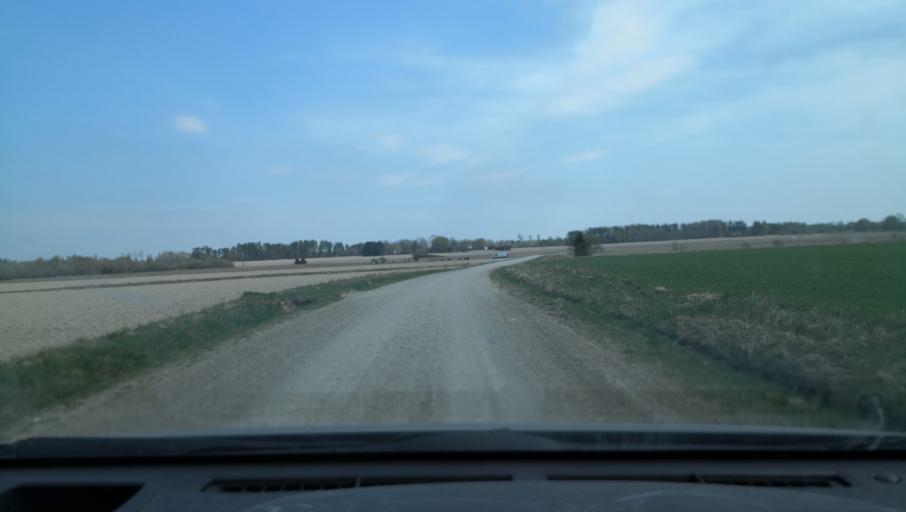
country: SE
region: Vaestmanland
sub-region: Vasteras
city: Skultuna
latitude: 59.7829
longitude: 16.4386
